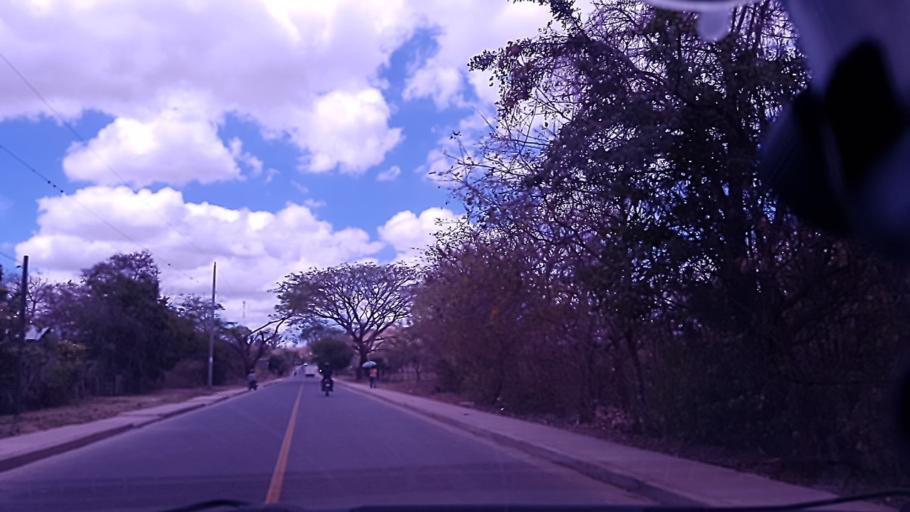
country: NI
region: Esteli
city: Condega
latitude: 13.3746
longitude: -86.3937
